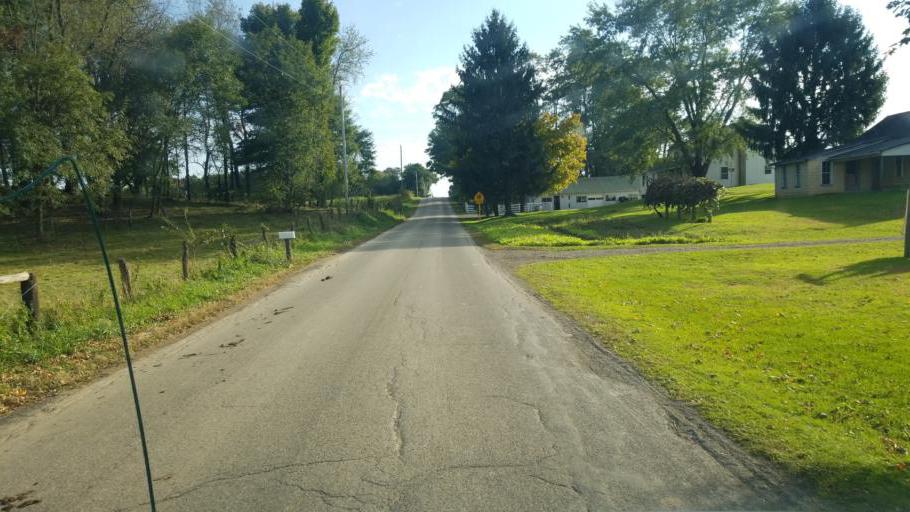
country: US
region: Ohio
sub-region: Wayne County
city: Shreve
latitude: 40.6363
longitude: -82.0814
